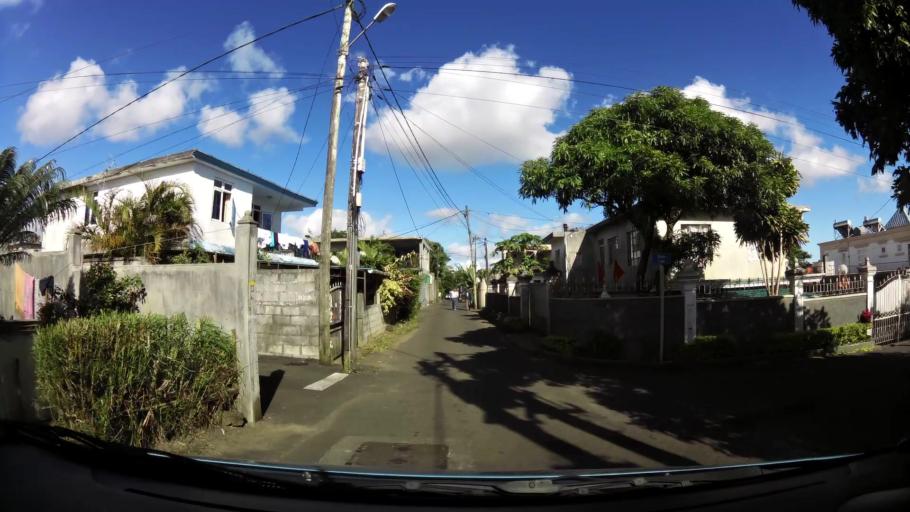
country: MU
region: Plaines Wilhems
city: Curepipe
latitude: -20.2991
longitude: 57.5112
